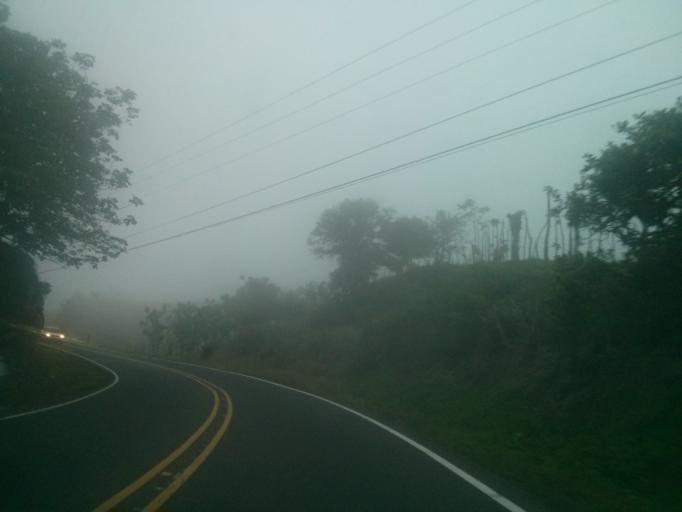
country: CR
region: Cartago
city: Cot
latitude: 9.9007
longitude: -83.8286
